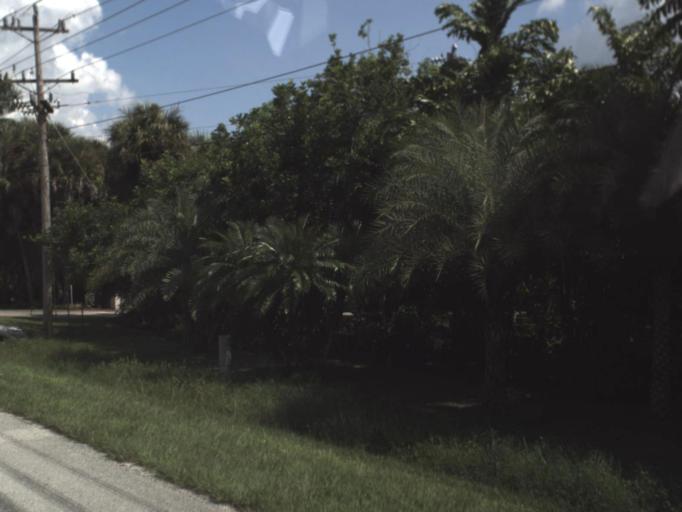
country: US
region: Florida
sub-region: Lee County
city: Fort Myers Shores
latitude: 26.7160
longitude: -81.7696
